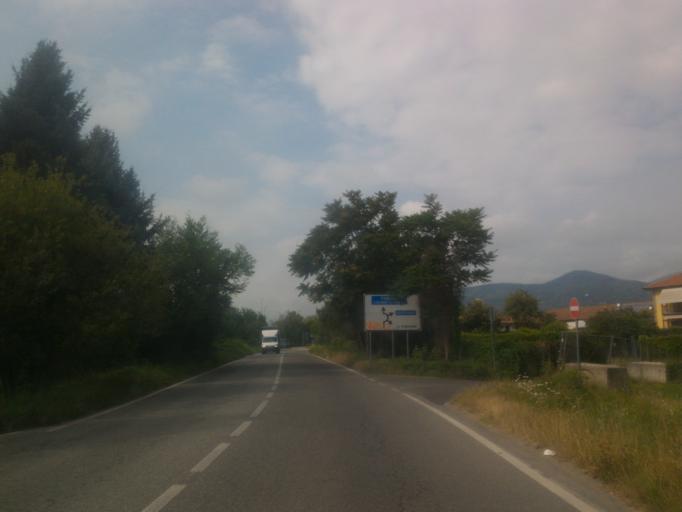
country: IT
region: Piedmont
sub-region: Provincia di Torino
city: Pinerolo
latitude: 44.8815
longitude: 7.3156
